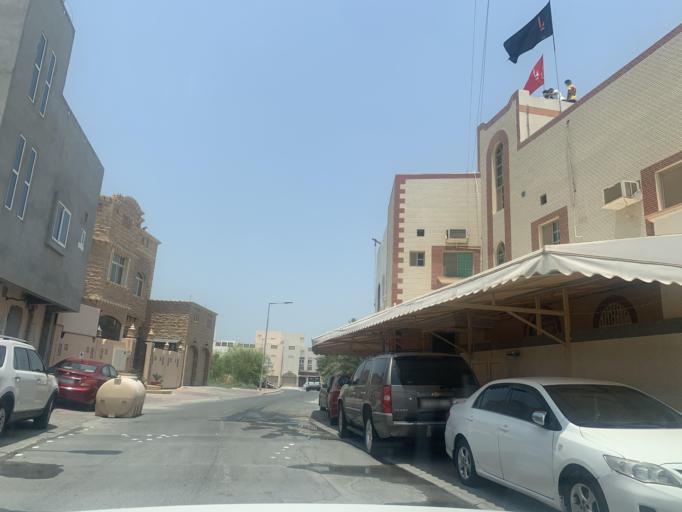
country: BH
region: Central Governorate
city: Madinat Hamad
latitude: 26.1448
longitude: 50.4596
